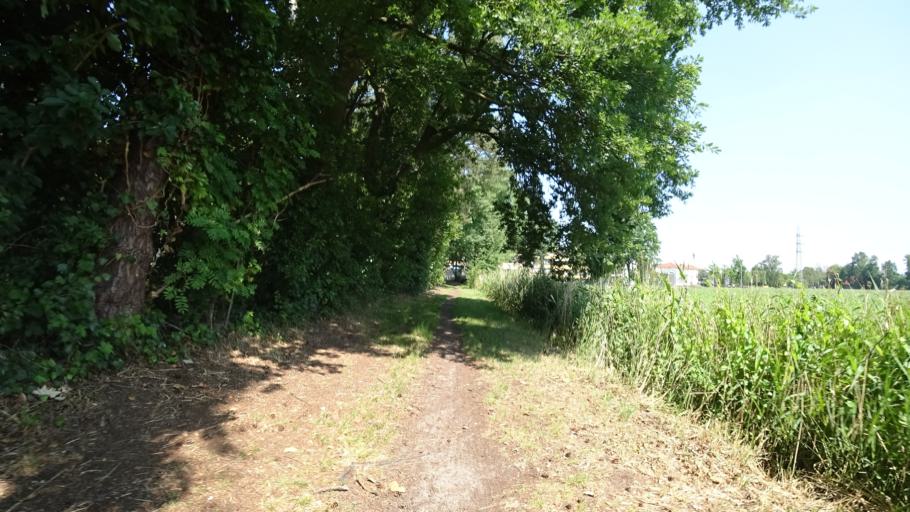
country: DE
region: North Rhine-Westphalia
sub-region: Regierungsbezirk Detmold
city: Guetersloh
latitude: 51.9314
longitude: 8.3687
